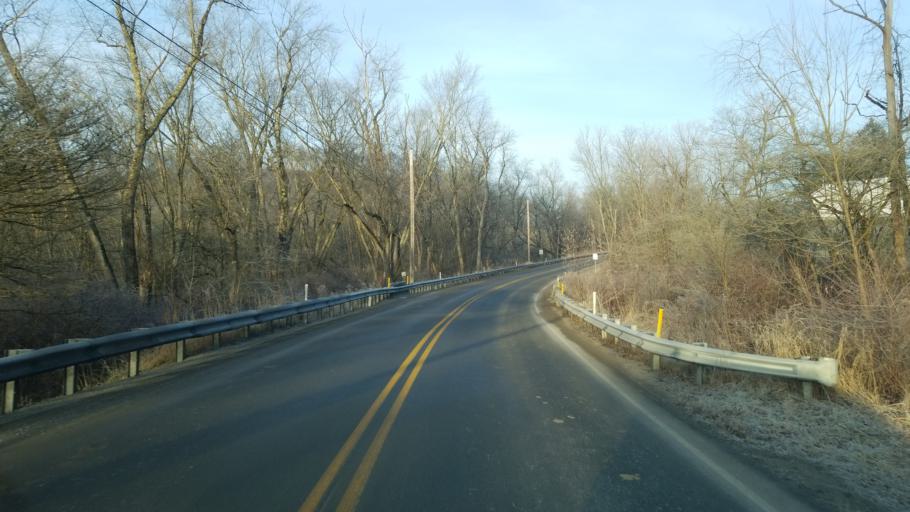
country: US
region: Pennsylvania
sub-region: Jefferson County
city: Punxsutawney
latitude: 40.8637
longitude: -79.1619
